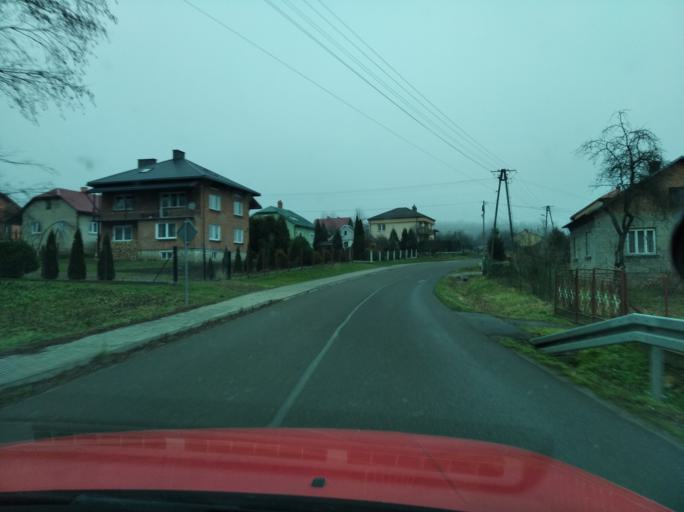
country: PL
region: Subcarpathian Voivodeship
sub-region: Powiat przemyski
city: Nienadowa
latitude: 49.8254
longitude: 22.4229
